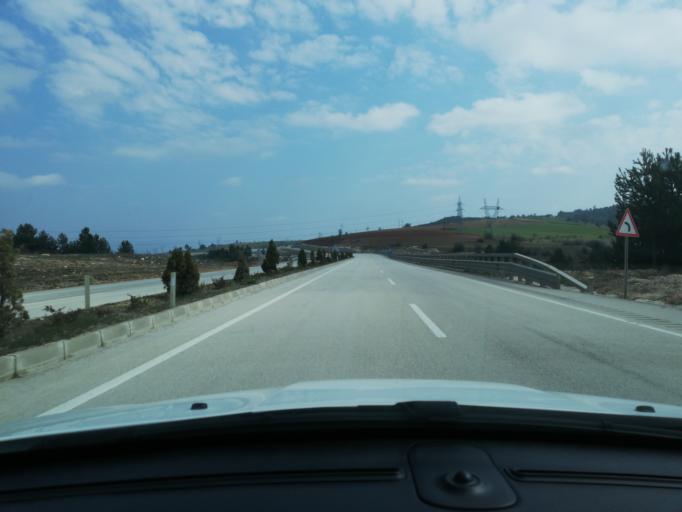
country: TR
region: Kastamonu
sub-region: Cide
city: Kastamonu
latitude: 41.3780
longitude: 33.8037
